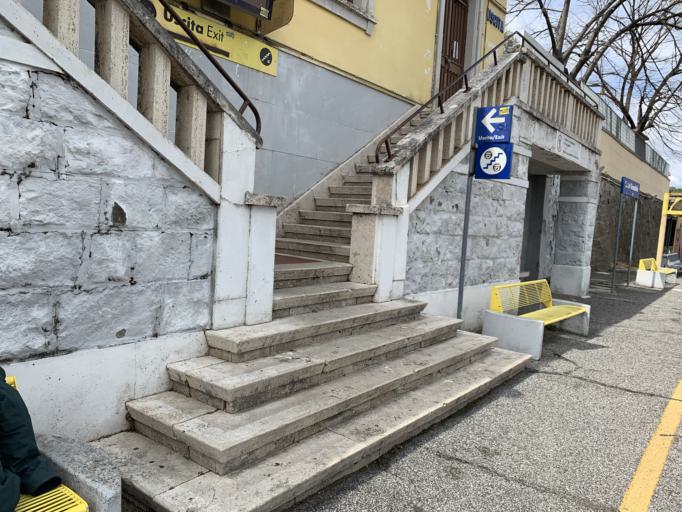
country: IT
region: Latium
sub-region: Citta metropolitana di Roma Capitale
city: Castel Gandolfo
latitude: 41.7469
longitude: 12.6522
